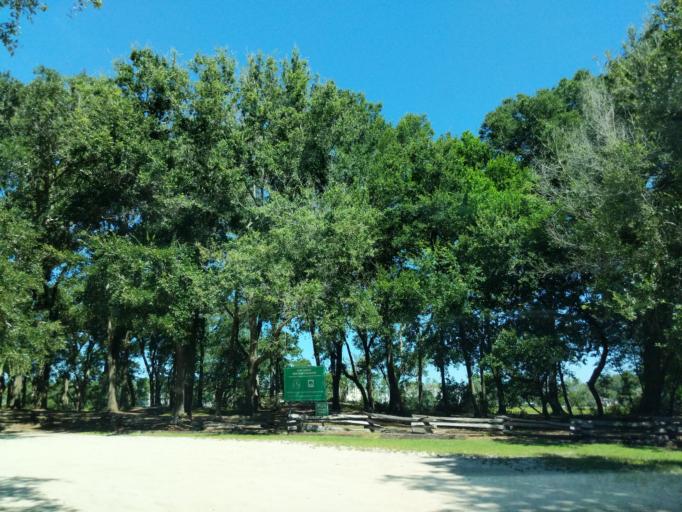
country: US
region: South Carolina
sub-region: Charleston County
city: Folly Beach
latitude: 32.7050
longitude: -79.9458
